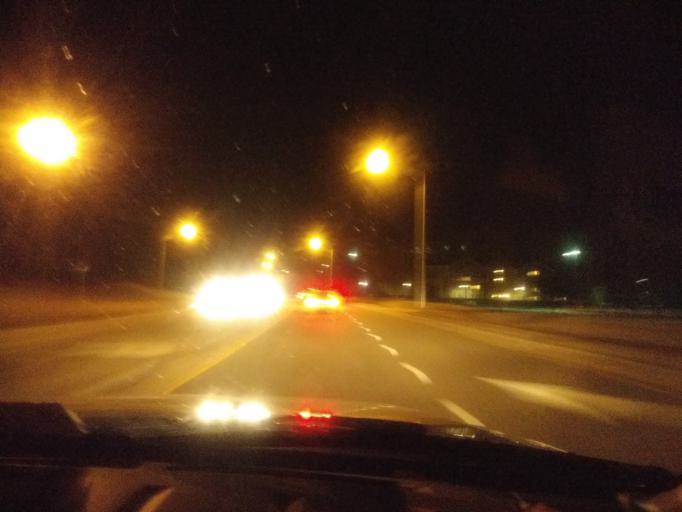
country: US
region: Virginia
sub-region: City of Chesapeake
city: Chesapeake
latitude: 36.7982
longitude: -76.1912
